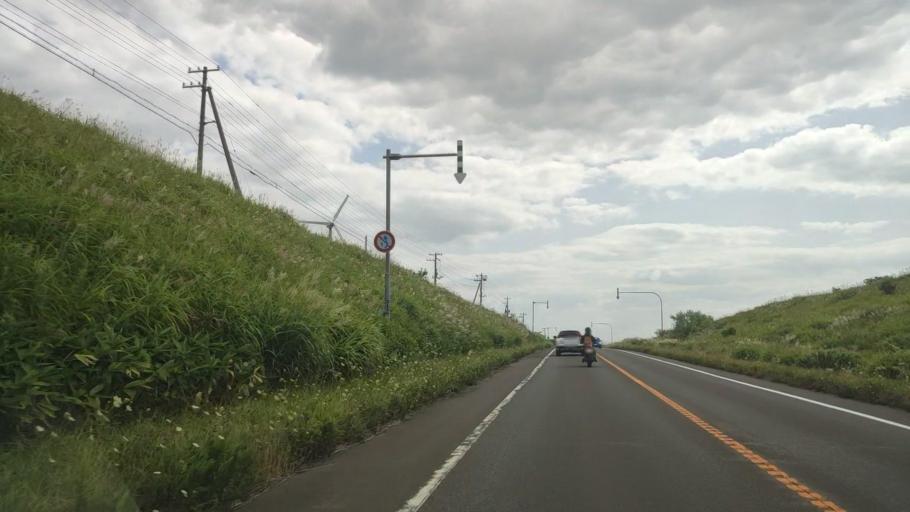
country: JP
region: Hokkaido
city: Rumoi
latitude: 44.5158
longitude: 141.7662
